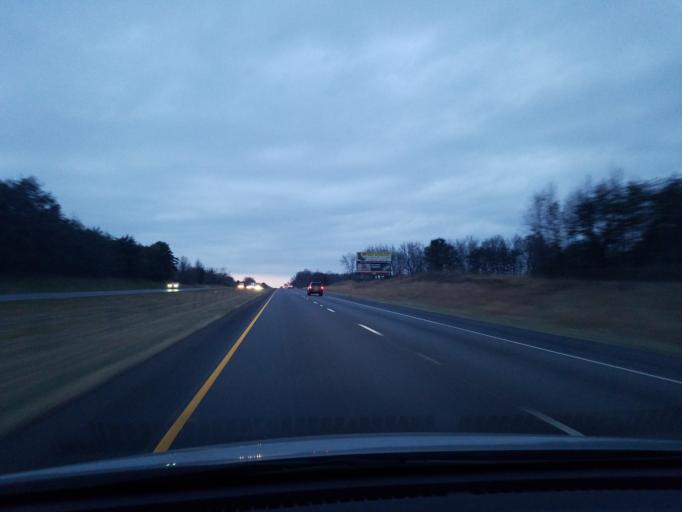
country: US
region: Indiana
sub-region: Scott County
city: Scottsburg
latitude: 38.6361
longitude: -85.7838
